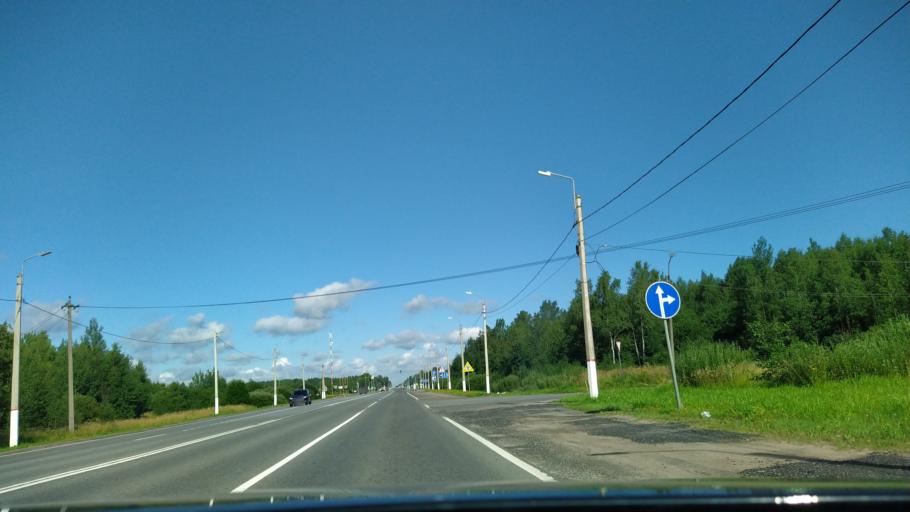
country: RU
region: Leningrad
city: Tosno
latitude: 59.5663
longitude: 30.8309
